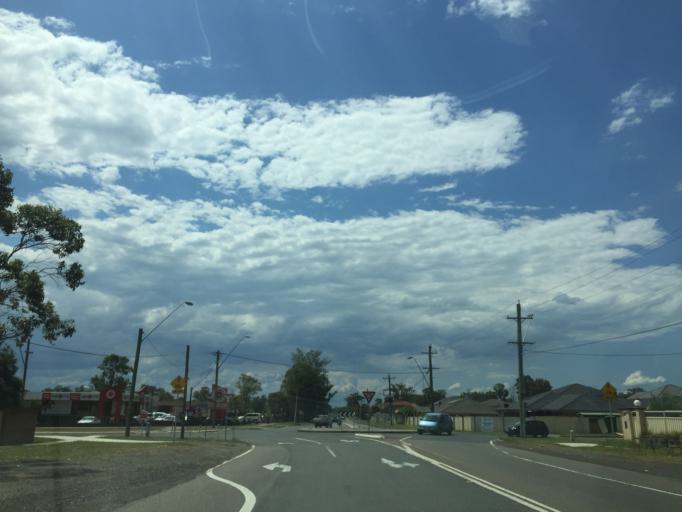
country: AU
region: New South Wales
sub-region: Blacktown
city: Glendenning
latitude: -33.7450
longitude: 150.8426
